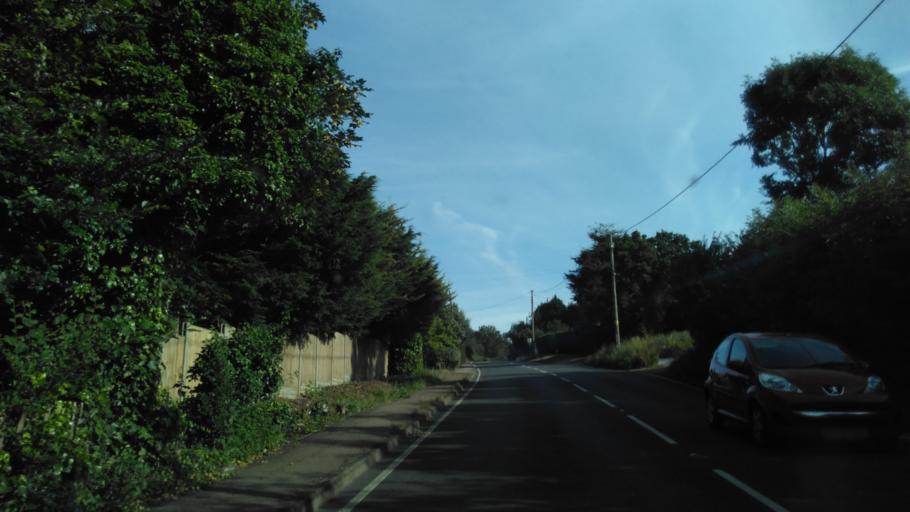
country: GB
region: England
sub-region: Kent
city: Whitstable
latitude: 51.3352
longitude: 1.0227
